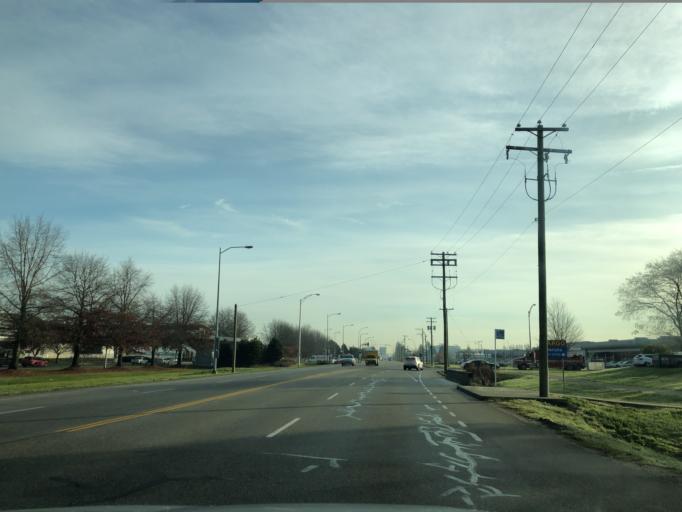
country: CA
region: British Columbia
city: Richmond
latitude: 49.1922
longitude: -123.1600
